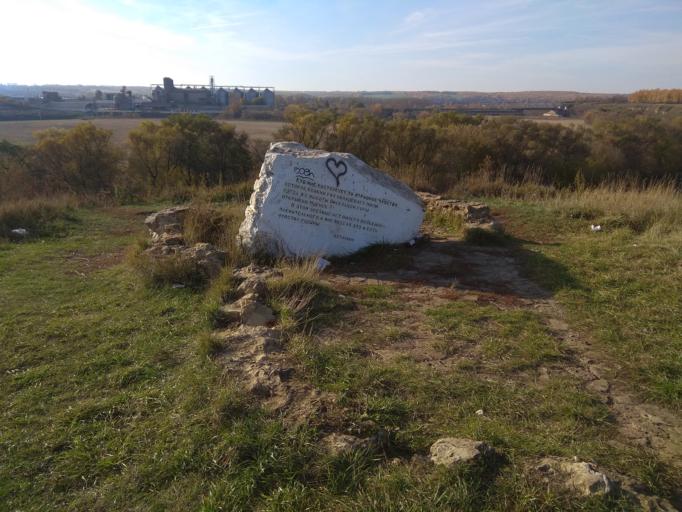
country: RU
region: Orjol
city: Mtsensk
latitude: 53.2994
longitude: 36.5807
